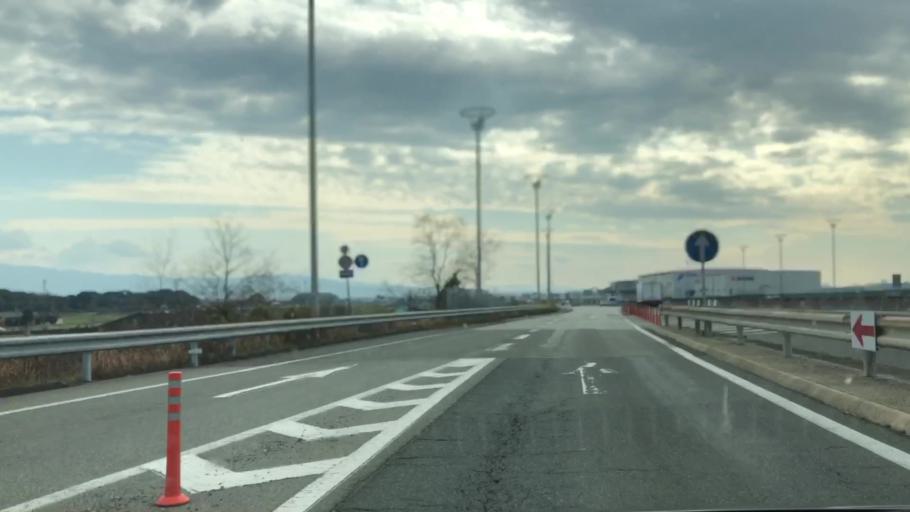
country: JP
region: Saga Prefecture
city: Tosu
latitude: 33.3945
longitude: 130.5386
